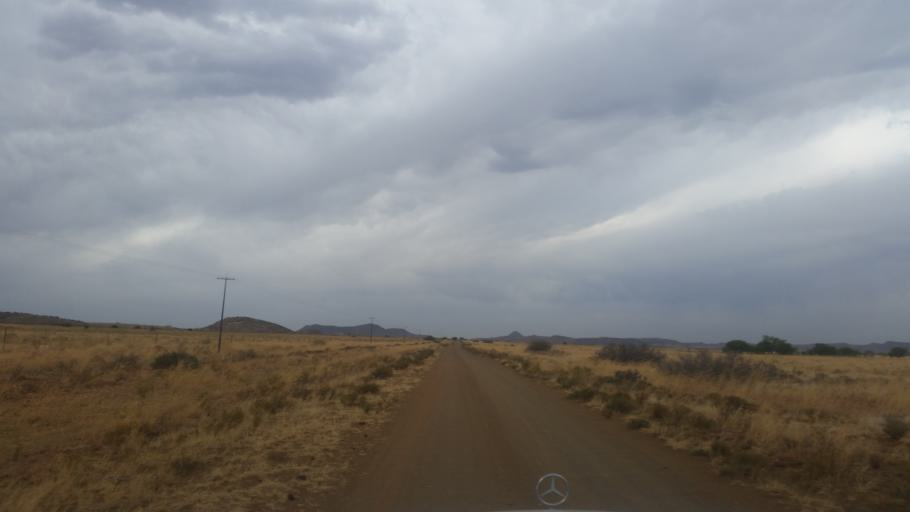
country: ZA
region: Orange Free State
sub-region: Xhariep District Municipality
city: Trompsburg
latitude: -30.5064
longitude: 25.9411
